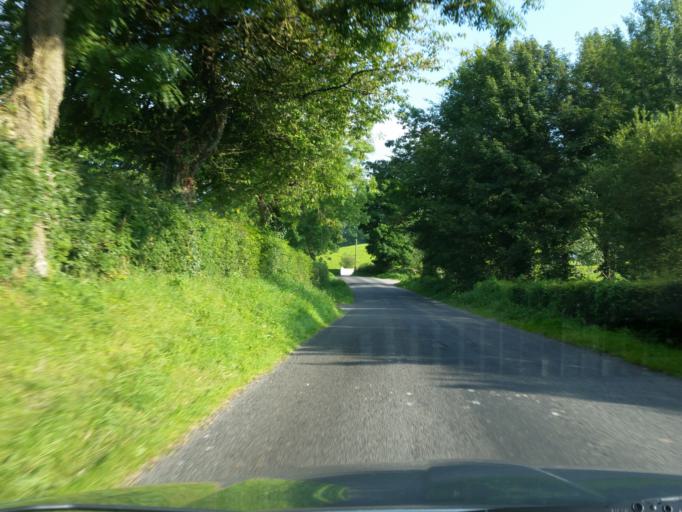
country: GB
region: Northern Ireland
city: Lisnaskea
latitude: 54.2852
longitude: -7.4390
